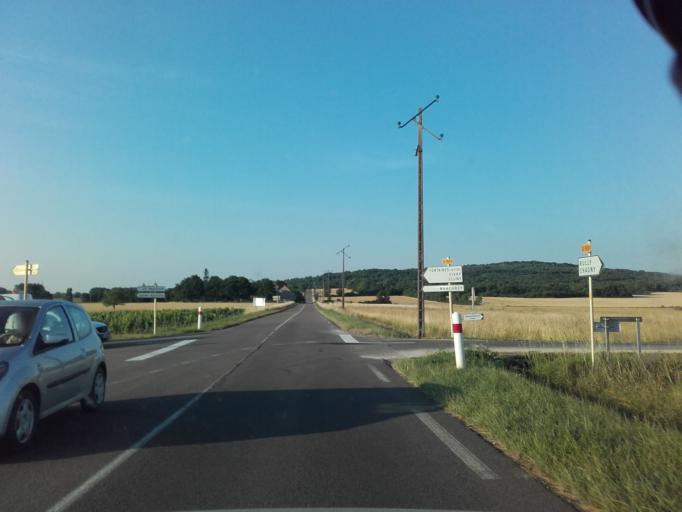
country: FR
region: Bourgogne
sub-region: Departement de Saone-et-Loire
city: Rully
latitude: 46.8656
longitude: 4.7524
